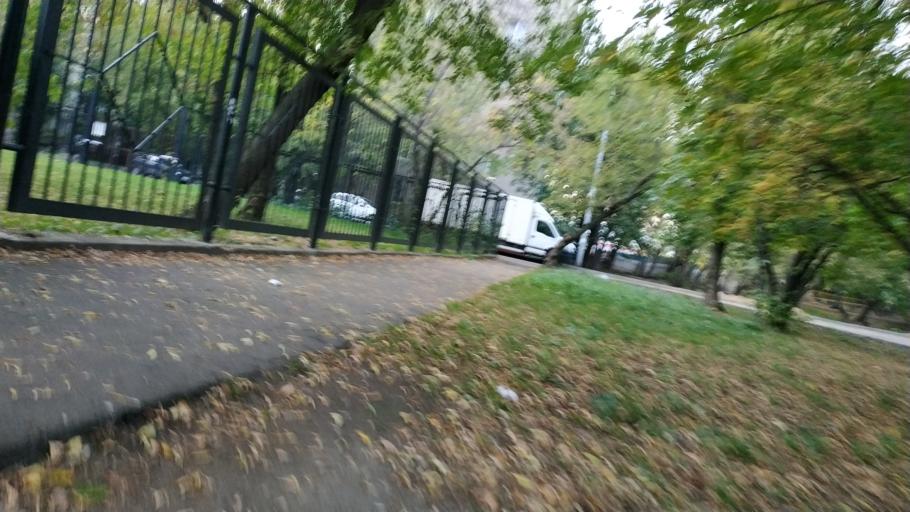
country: RU
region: Moscow
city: Tekstil'shchiki
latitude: 55.7323
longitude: 37.7237
